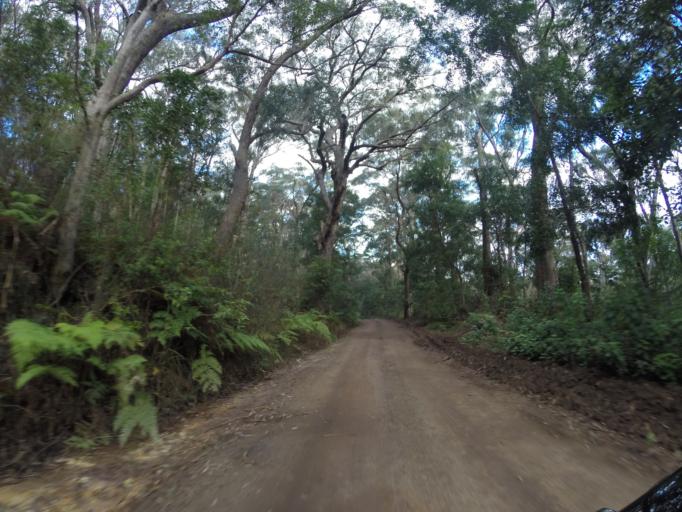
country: AU
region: New South Wales
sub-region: Wollongong
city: Cordeaux Heights
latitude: -34.4335
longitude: 150.7860
